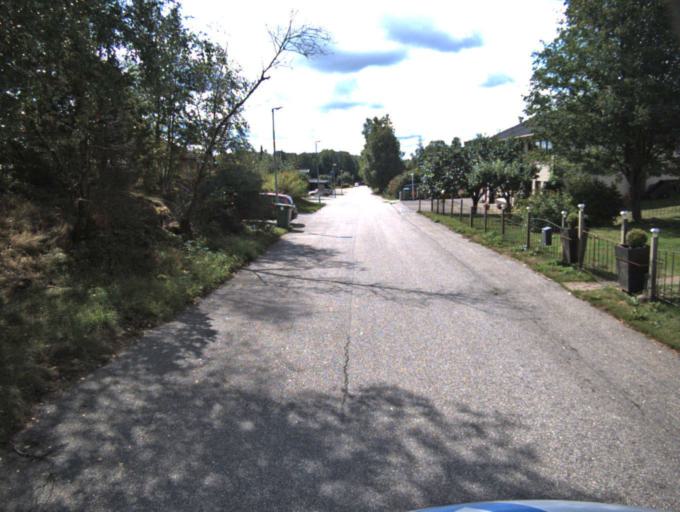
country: SE
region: Vaestra Goetaland
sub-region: Ulricehamns Kommun
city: Ulricehamn
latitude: 57.7010
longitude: 13.4993
